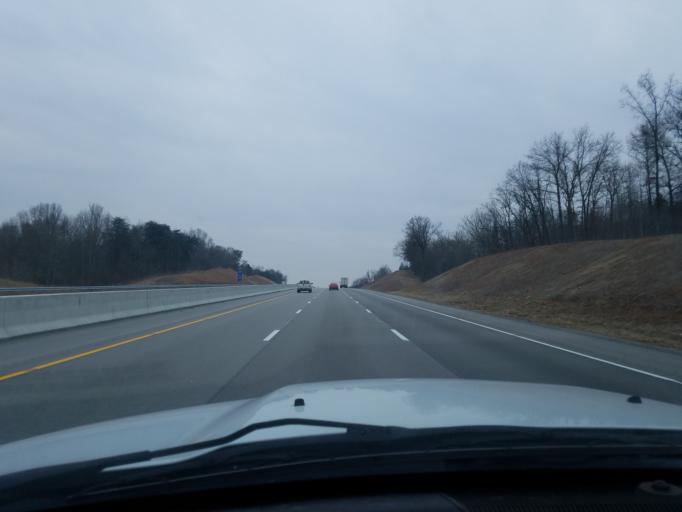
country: US
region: Kentucky
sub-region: Hart County
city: Munfordville
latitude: 37.3275
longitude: -85.9068
